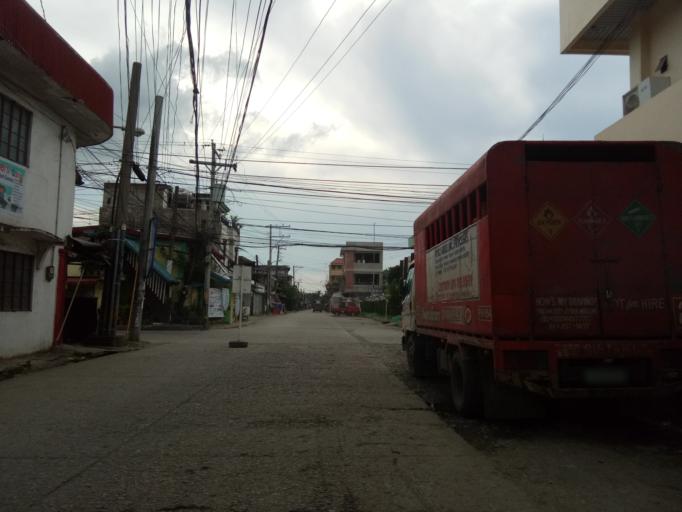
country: PH
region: Caraga
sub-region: Province of Surigao del Norte
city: Surigao
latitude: 9.7851
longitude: 125.4880
